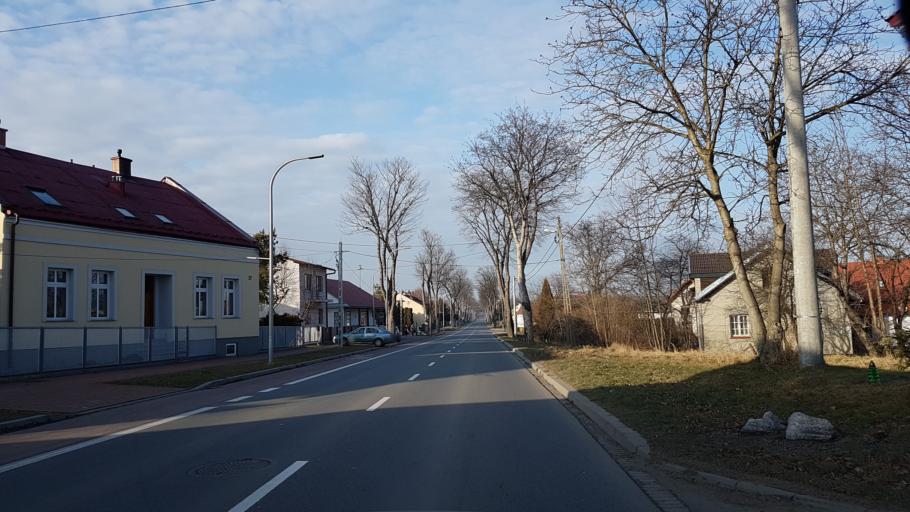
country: PL
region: Lesser Poland Voivodeship
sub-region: Powiat nowosadecki
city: Stary Sacz
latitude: 49.5494
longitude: 20.6413
